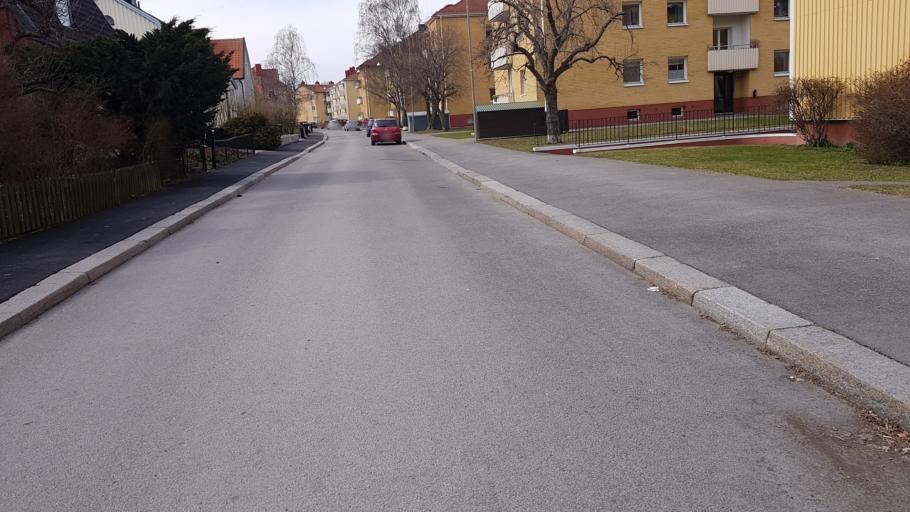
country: SE
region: OEstergoetland
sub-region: Norrkopings Kommun
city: Norrkoping
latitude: 58.5882
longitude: 16.2143
